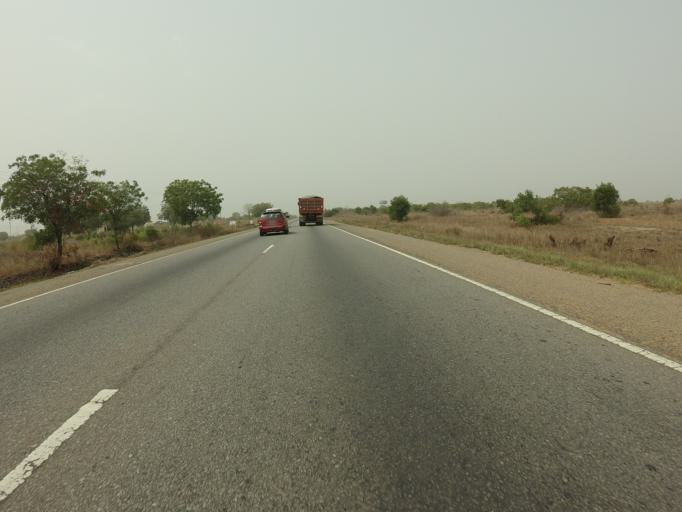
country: GH
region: Greater Accra
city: Tema
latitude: 5.8702
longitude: 0.3229
